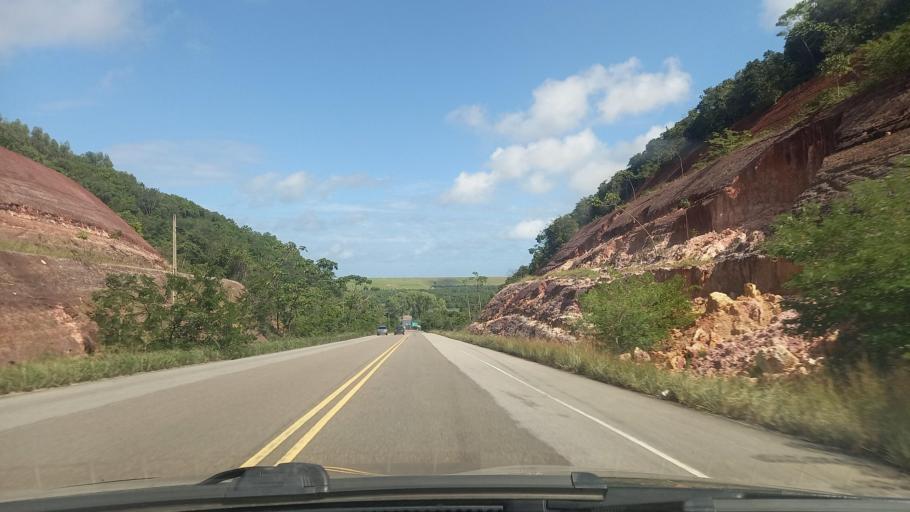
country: BR
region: Alagoas
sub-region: Marechal Deodoro
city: Marechal Deodoro
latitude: -9.8325
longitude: -35.9294
